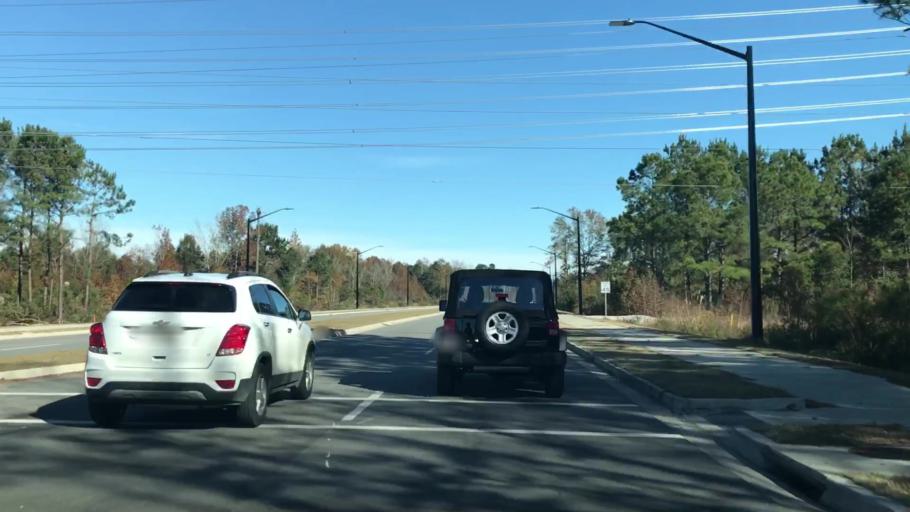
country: US
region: South Carolina
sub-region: Dorchester County
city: Summerville
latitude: 33.0427
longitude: -80.1814
